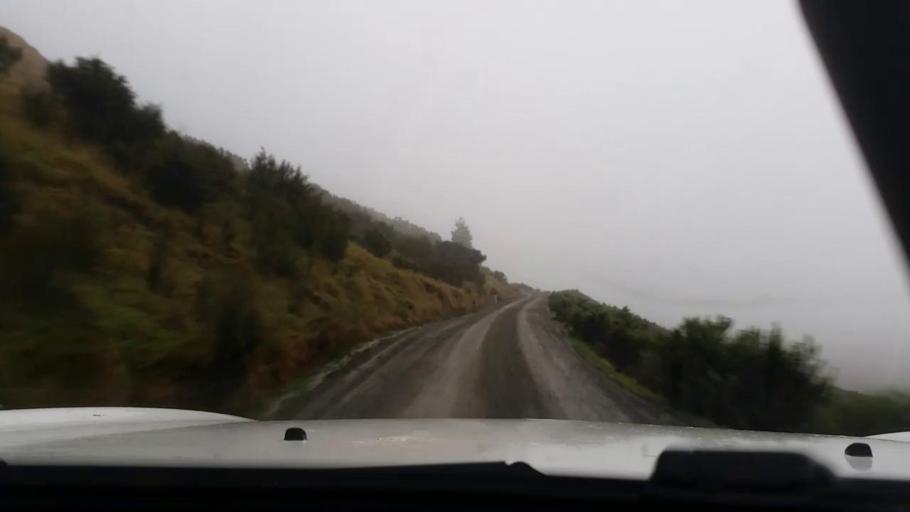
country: NZ
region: Wellington
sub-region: Masterton District
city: Masterton
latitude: -41.2467
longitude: 175.8780
